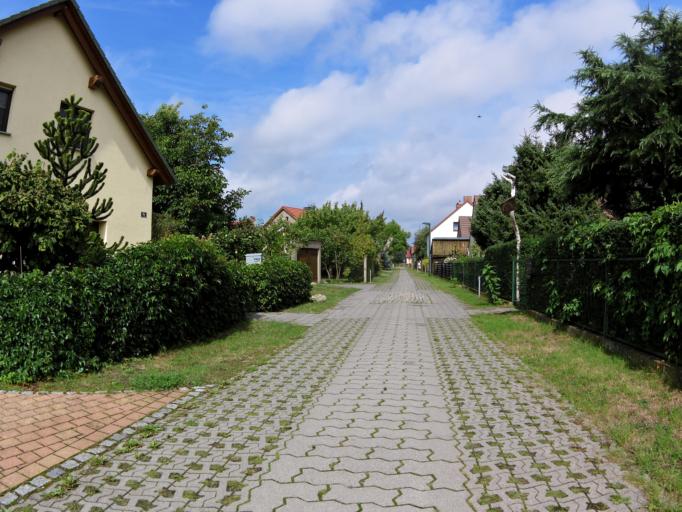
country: DE
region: Brandenburg
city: Storkow
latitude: 52.2763
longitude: 13.9294
